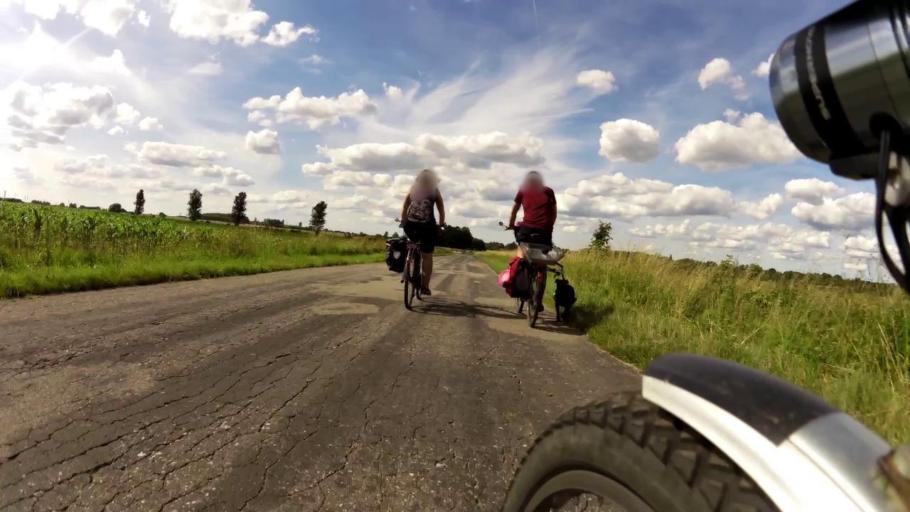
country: PL
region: West Pomeranian Voivodeship
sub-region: Powiat lobeski
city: Dobra
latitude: 53.5770
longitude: 15.4001
